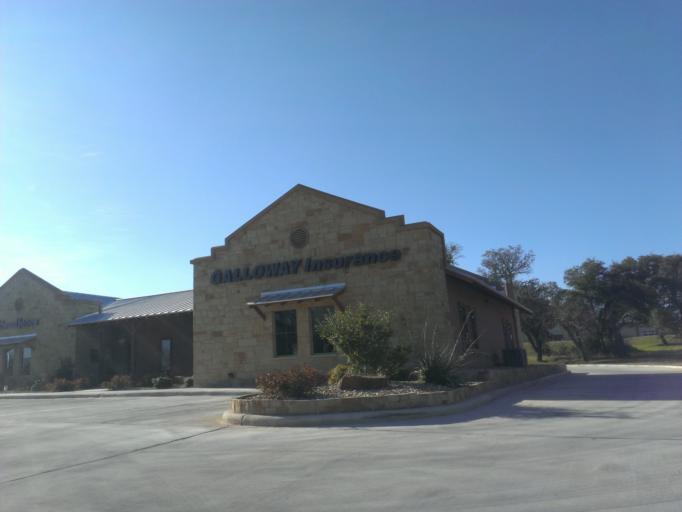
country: US
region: Texas
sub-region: Burnet County
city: Burnet
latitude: 30.7464
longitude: -98.2309
